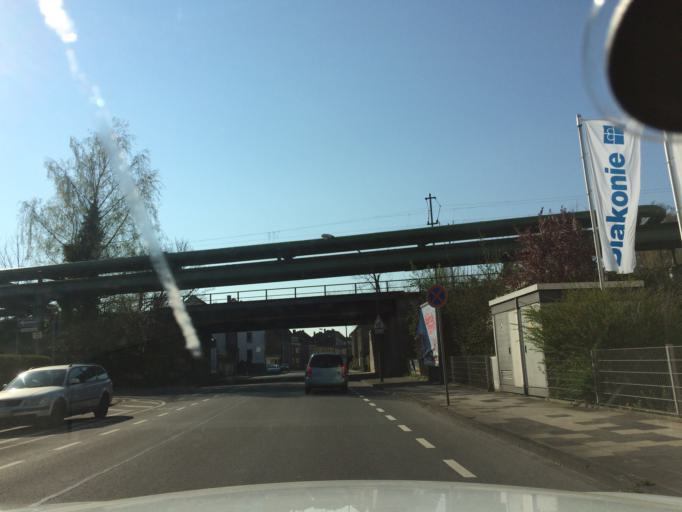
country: DE
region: North Rhine-Westphalia
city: Marl
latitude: 51.6047
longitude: 7.0903
